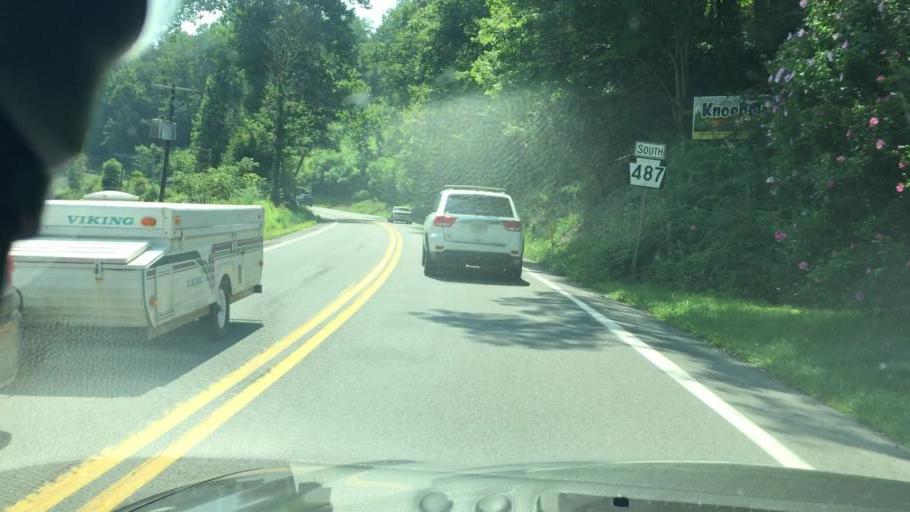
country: US
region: Pennsylvania
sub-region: Columbia County
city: Catawissa
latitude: 40.9422
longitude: -76.4565
